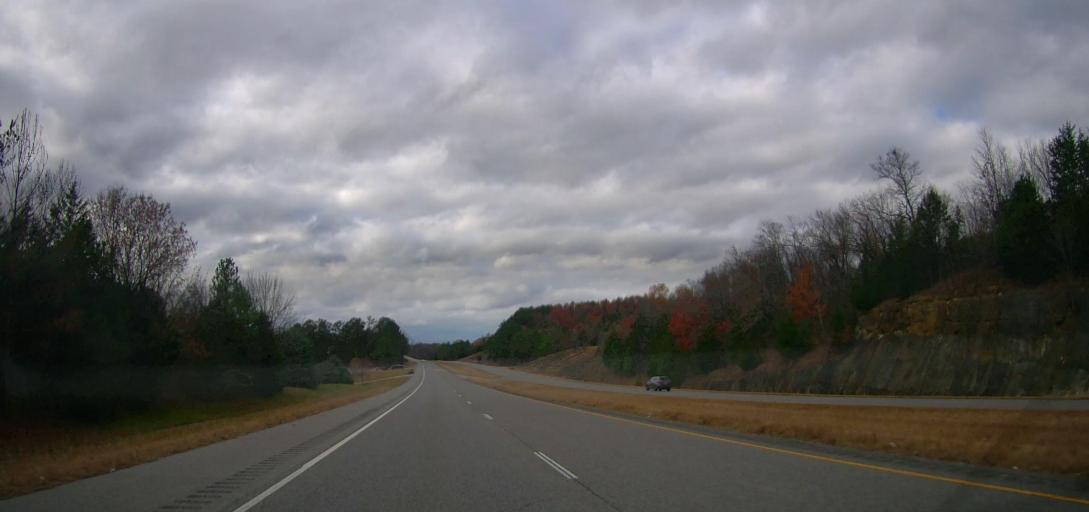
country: US
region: Alabama
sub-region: Lawrence County
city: Town Creek
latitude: 34.6245
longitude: -87.4737
